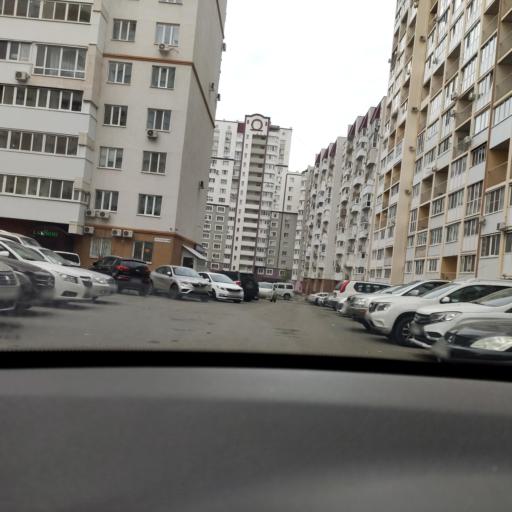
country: RU
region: Samara
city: Samara
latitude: 53.2229
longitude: 50.1945
